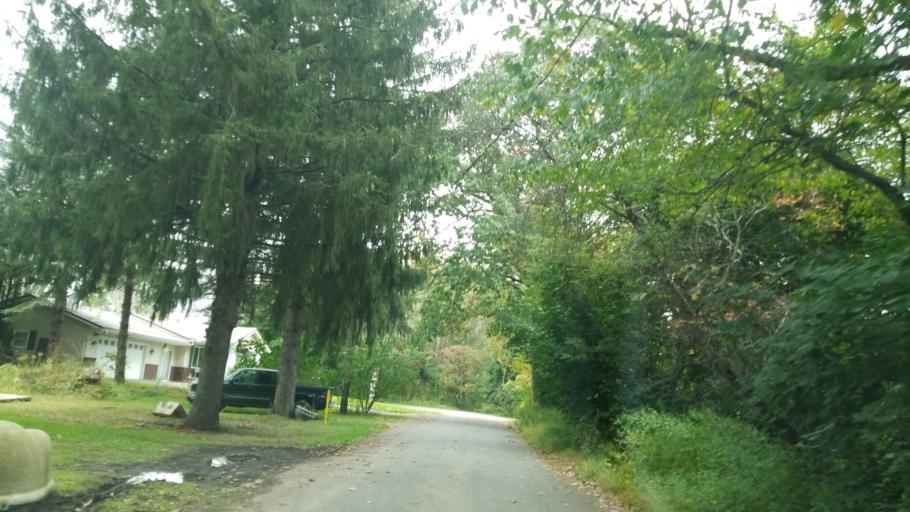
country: US
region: Pennsylvania
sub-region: Clearfield County
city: Hyde
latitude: 40.9978
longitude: -78.4637
